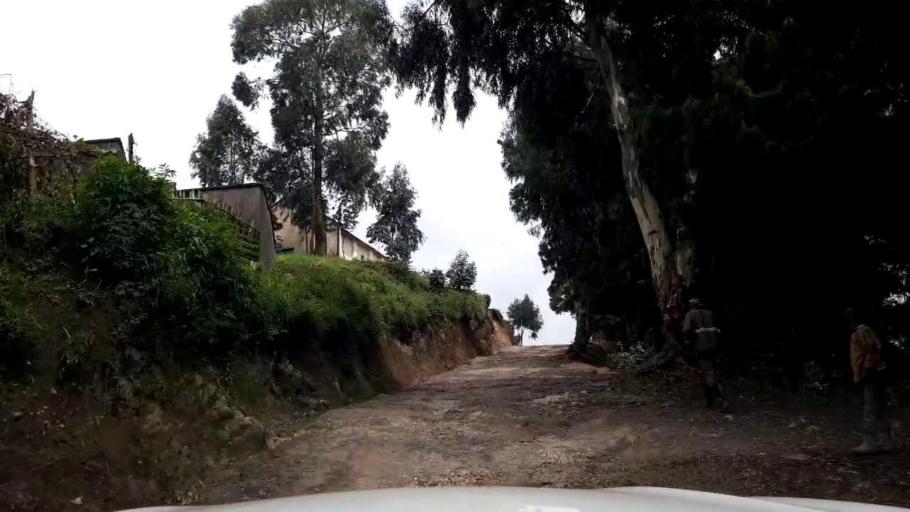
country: RW
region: Western Province
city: Kibuye
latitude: -1.9376
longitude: 29.4621
